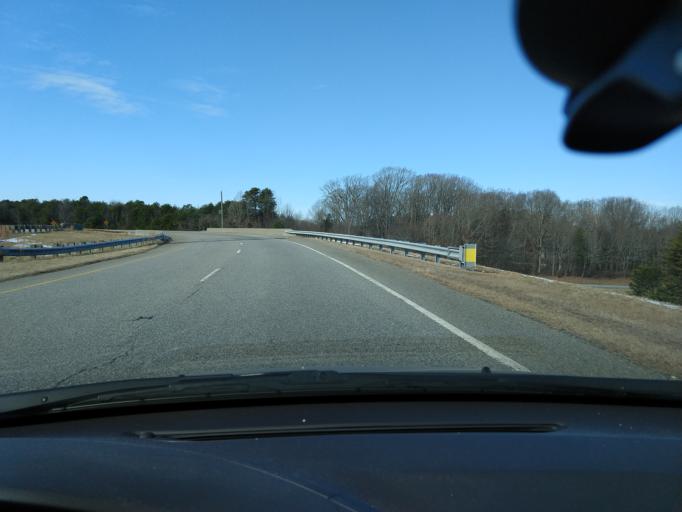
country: US
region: North Carolina
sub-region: Guilford County
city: Oak Ridge
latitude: 36.1094
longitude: -79.9631
